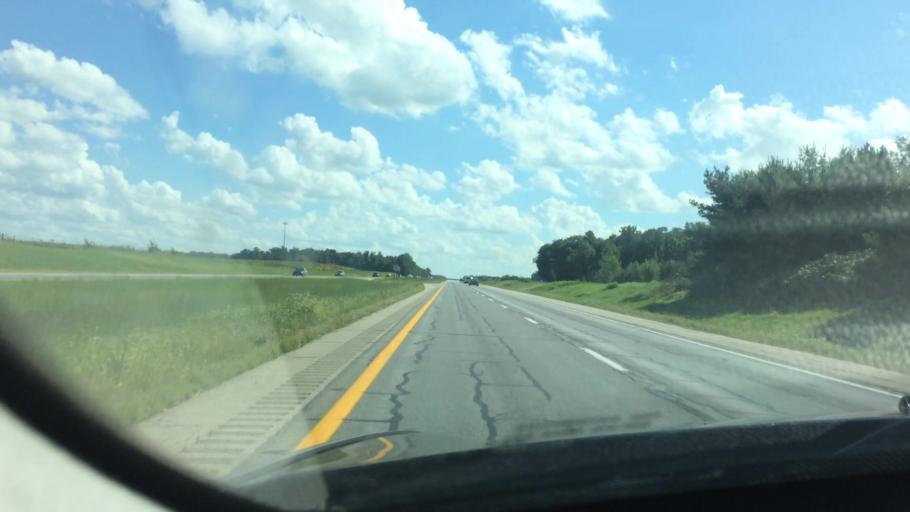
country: US
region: Ohio
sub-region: Auglaize County
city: Wapakoneta
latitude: 40.5254
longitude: -84.1696
